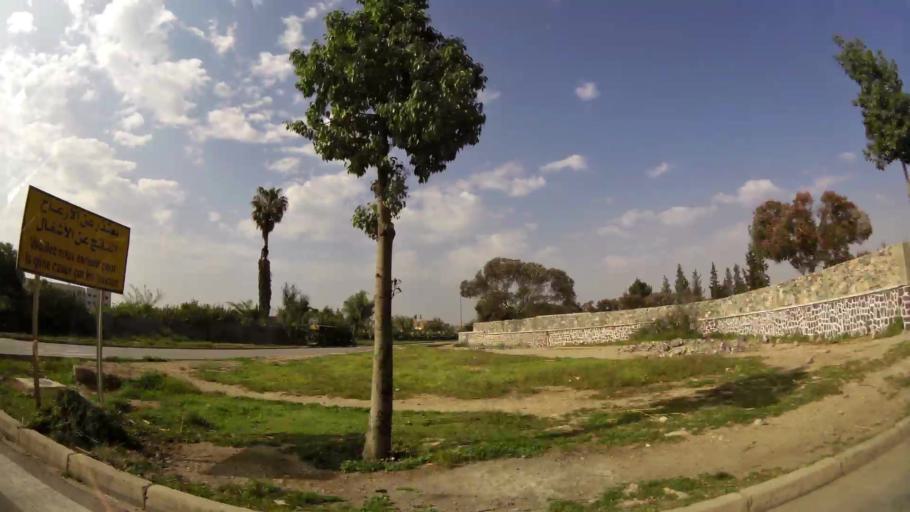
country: MA
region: Oriental
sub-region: Oujda-Angad
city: Oujda
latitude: 34.6918
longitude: -1.8969
